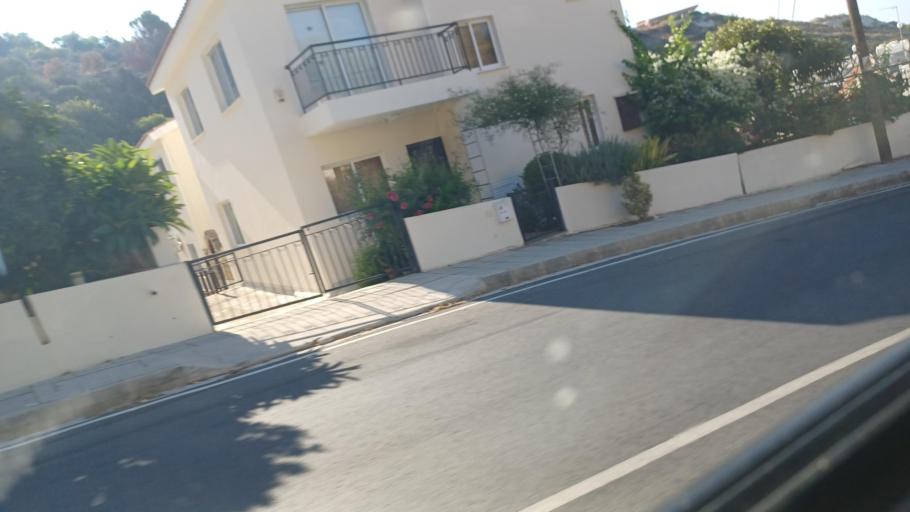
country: CY
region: Pafos
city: Tala
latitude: 34.8403
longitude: 32.4400
